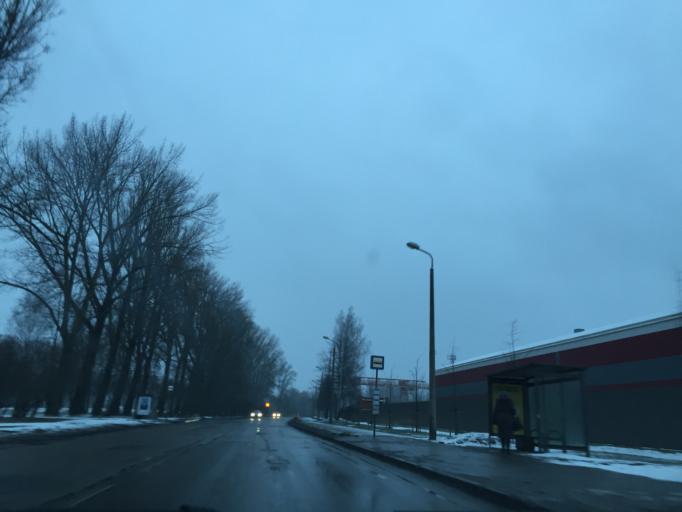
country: LV
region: Riga
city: Riga
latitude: 56.9708
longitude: 24.0732
